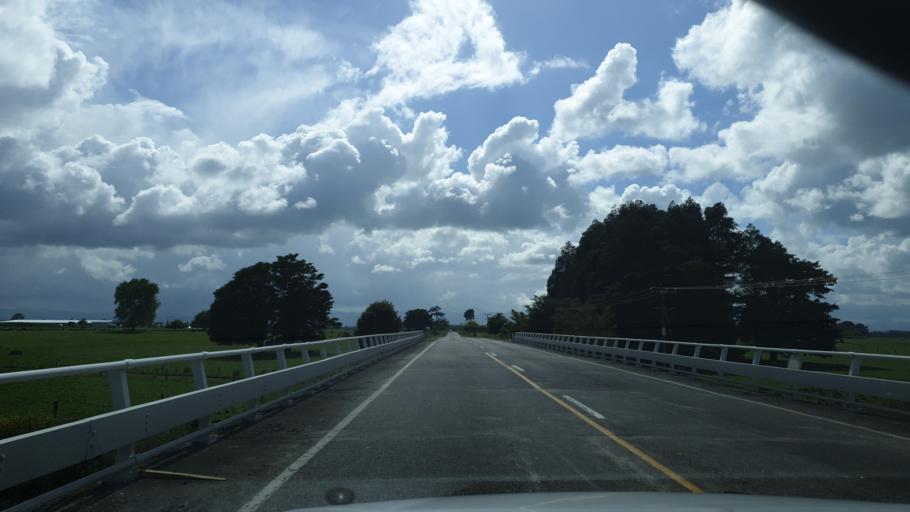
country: NZ
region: Waikato
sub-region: Hauraki District
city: Paeroa
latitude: -37.5142
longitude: 175.5059
